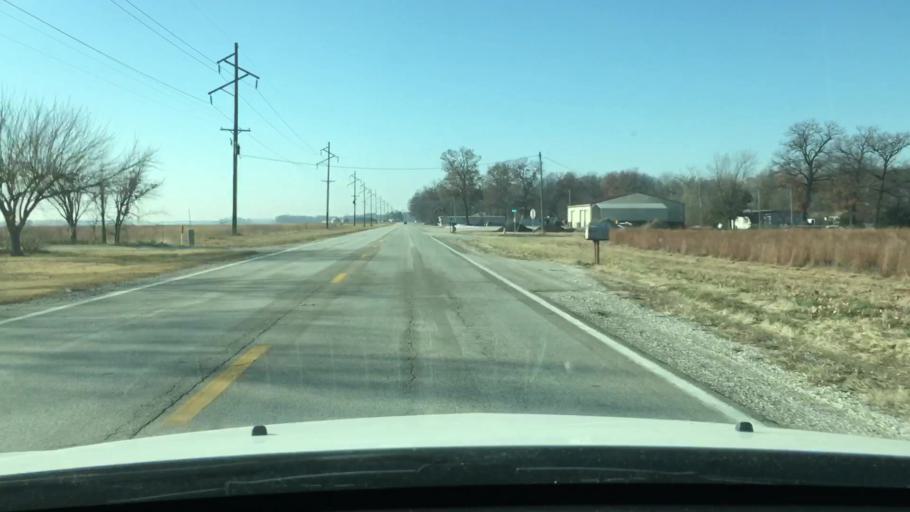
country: US
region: Illinois
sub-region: Cass County
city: Beardstown
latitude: 39.9852
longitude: -90.4454
